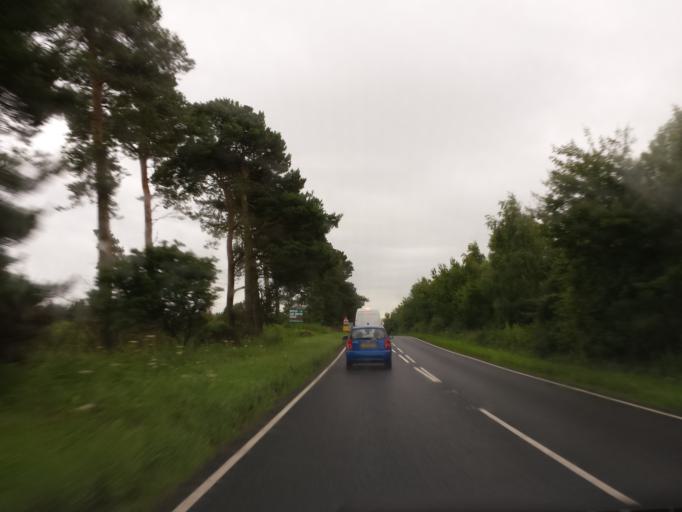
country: GB
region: Scotland
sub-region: Fife
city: Balmullo
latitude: 56.3969
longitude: -2.9089
